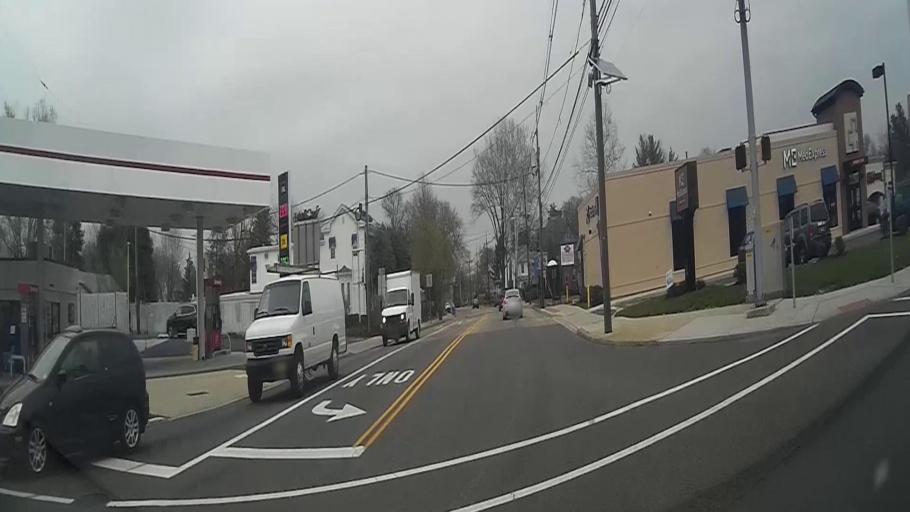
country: US
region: New Jersey
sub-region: Camden County
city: Mount Ephraim
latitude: 39.8815
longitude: -75.0859
